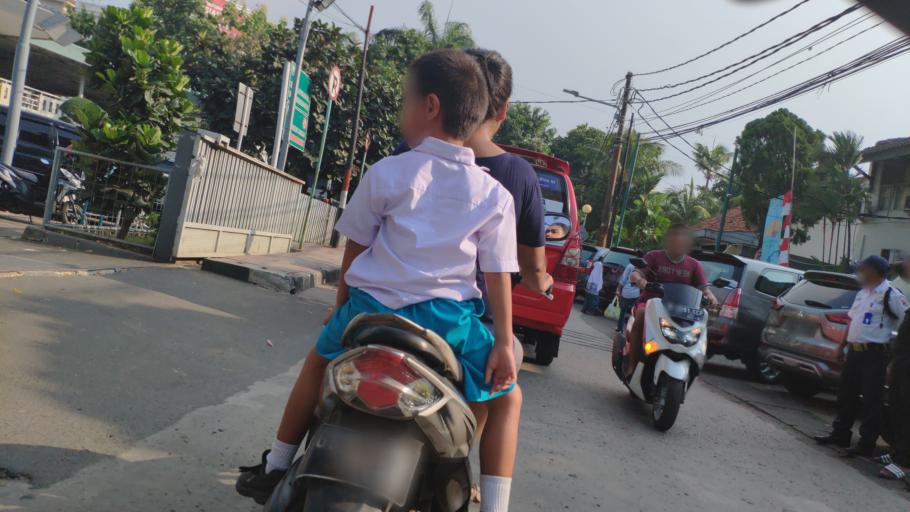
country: ID
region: Jakarta Raya
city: Jakarta
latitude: -6.2787
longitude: 106.7996
